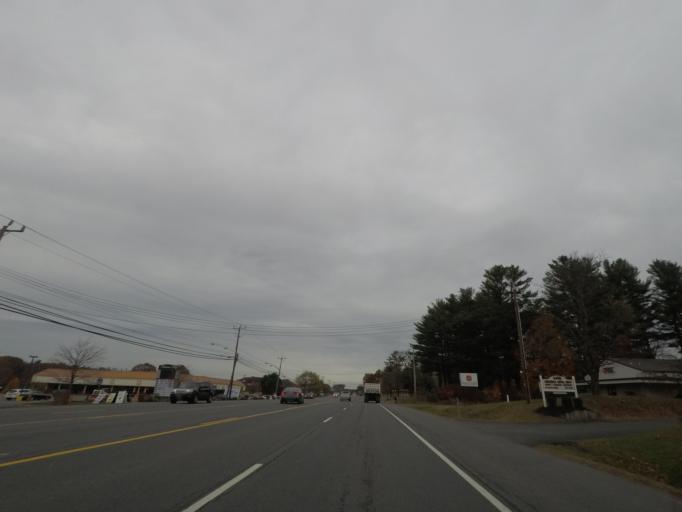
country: US
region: New York
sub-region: Saratoga County
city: Country Knolls
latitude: 42.8719
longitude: -73.7737
